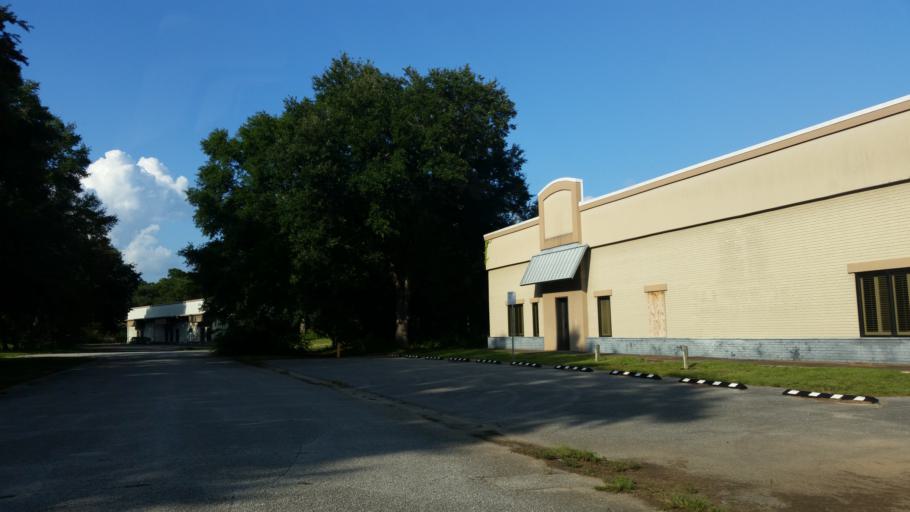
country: US
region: Florida
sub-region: Escambia County
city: Ferry Pass
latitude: 30.4814
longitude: -87.1950
